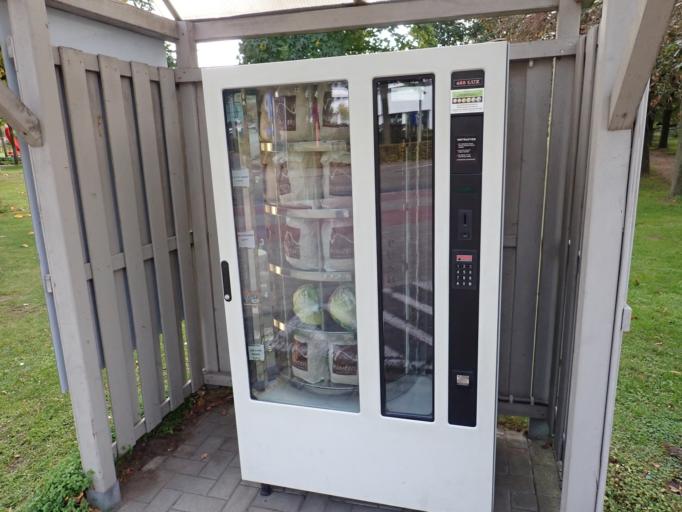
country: BE
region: Flanders
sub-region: Provincie Antwerpen
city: Zandhoven
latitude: 51.2742
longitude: 4.6435
